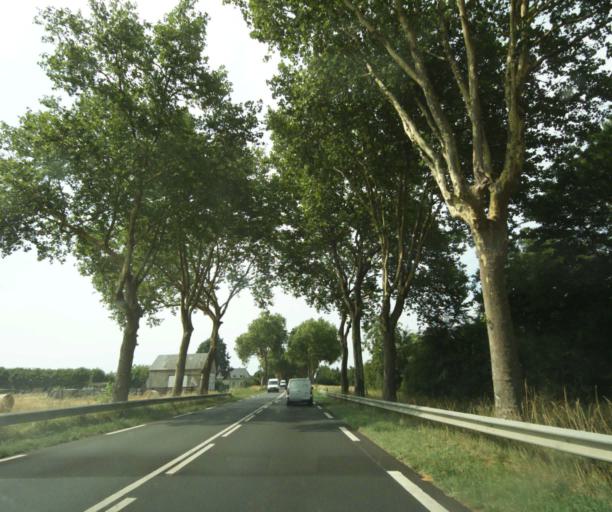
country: FR
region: Centre
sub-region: Departement d'Indre-et-Loire
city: La Membrolle-sur-Choisille
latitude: 47.4569
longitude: 0.6261
